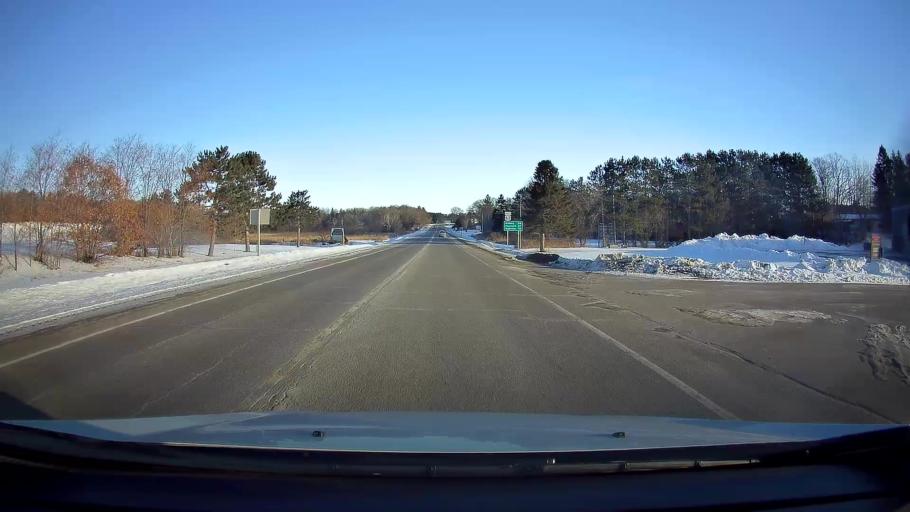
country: US
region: Wisconsin
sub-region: Washburn County
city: Spooner
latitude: 45.8342
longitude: -91.8830
